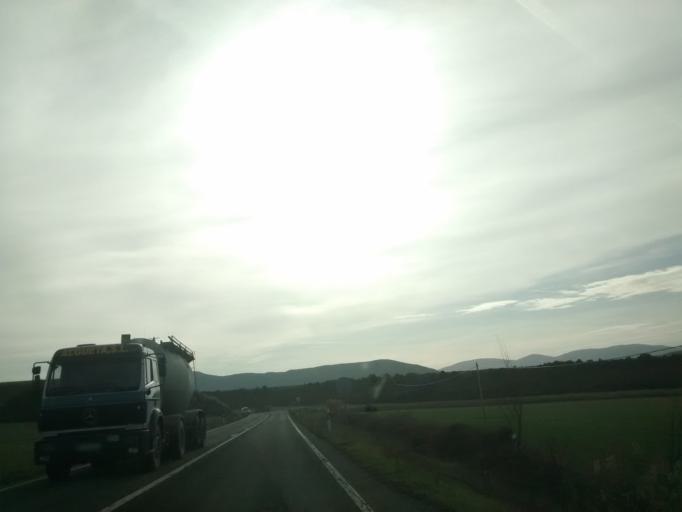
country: ES
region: Aragon
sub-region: Provincia de Huesca
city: Bailo
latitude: 42.5855
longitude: -0.8321
